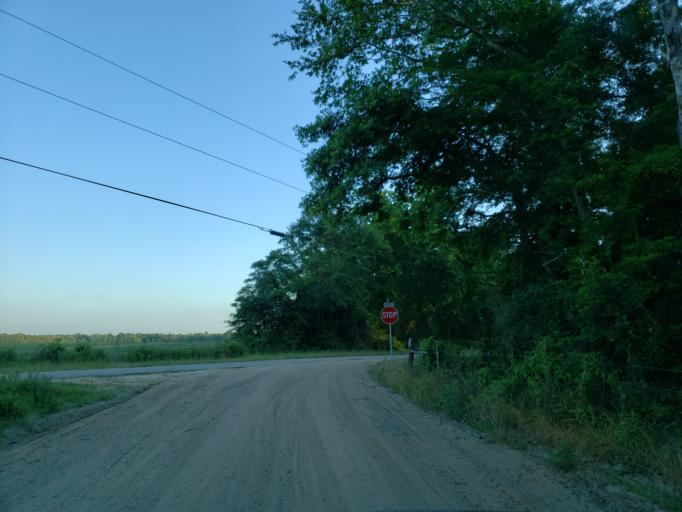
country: US
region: Georgia
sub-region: Crisp County
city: Cordele
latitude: 32.0257
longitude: -83.7484
